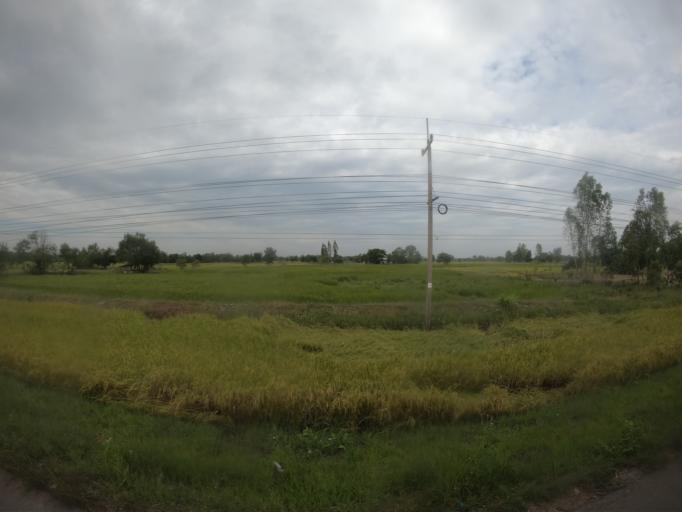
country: TH
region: Maha Sarakham
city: Kantharawichai
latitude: 16.3295
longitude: 103.2658
